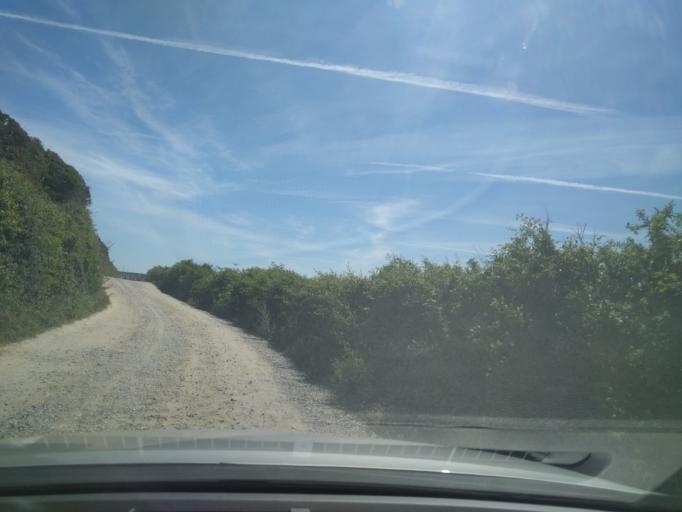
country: DK
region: South Denmark
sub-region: Kerteminde Kommune
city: Munkebo
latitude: 55.6088
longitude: 10.6007
